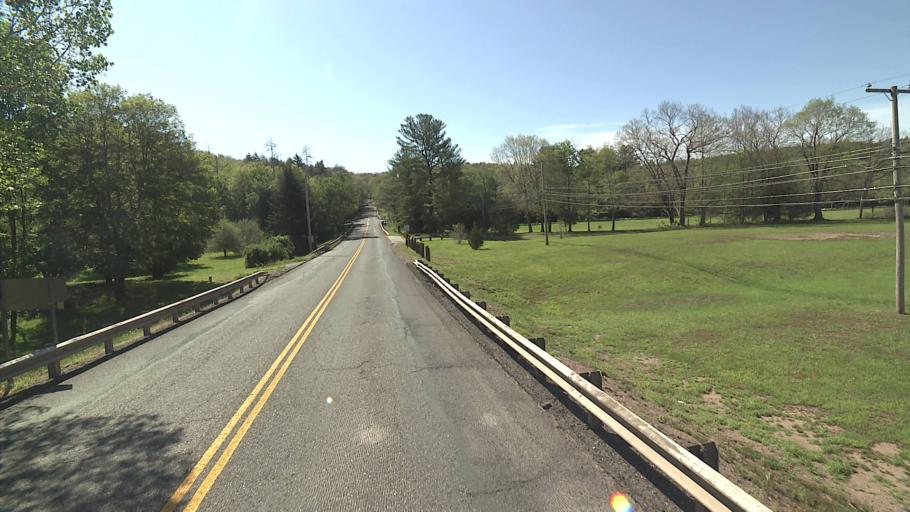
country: US
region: Connecticut
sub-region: Middlesex County
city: Moodus
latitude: 41.5521
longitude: -72.4486
